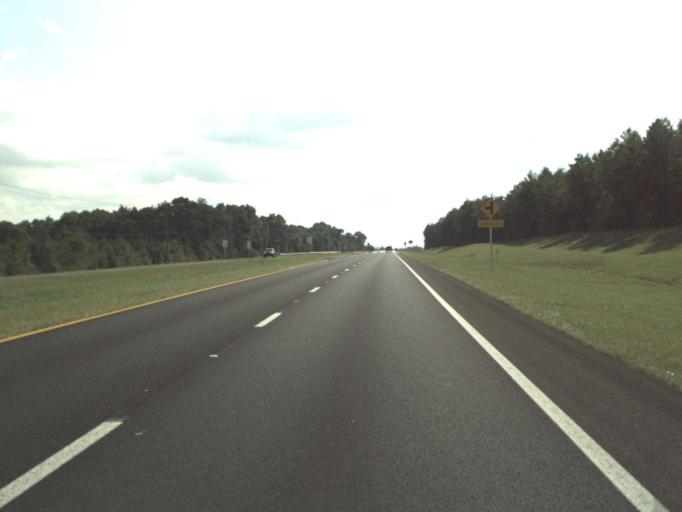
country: US
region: Florida
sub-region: Bay County
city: Laguna Beach
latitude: 30.5079
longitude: -85.8414
